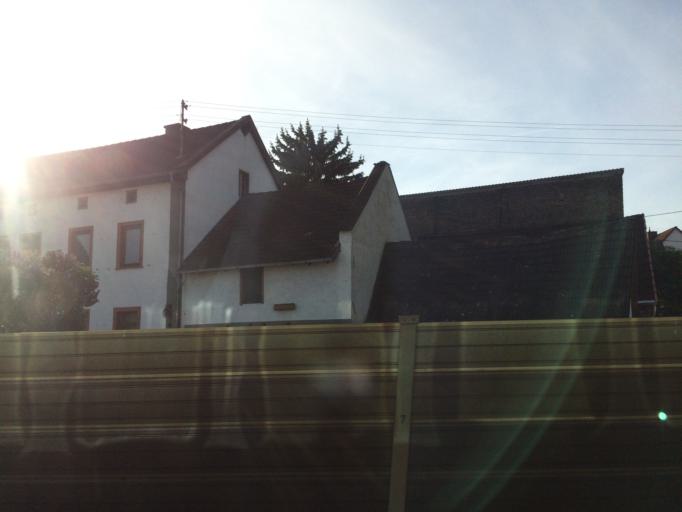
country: DE
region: Rheinland-Pfalz
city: Oestrich-Winkel
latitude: 50.0082
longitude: 8.0285
